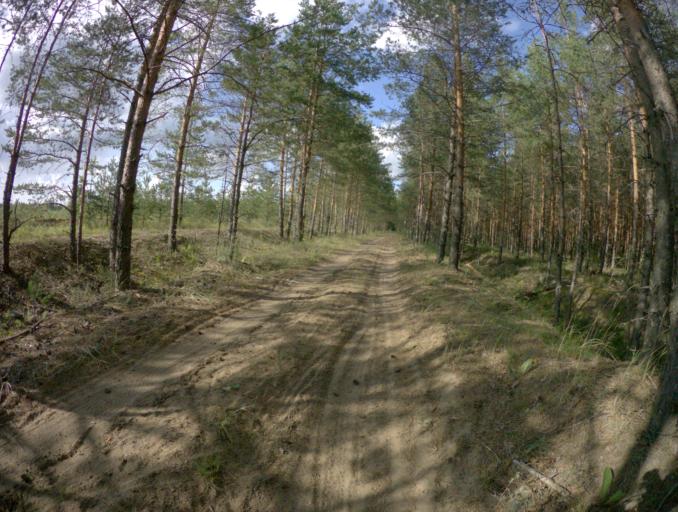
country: RU
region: Vladimir
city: Sobinka
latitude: 55.9568
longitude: 40.0610
